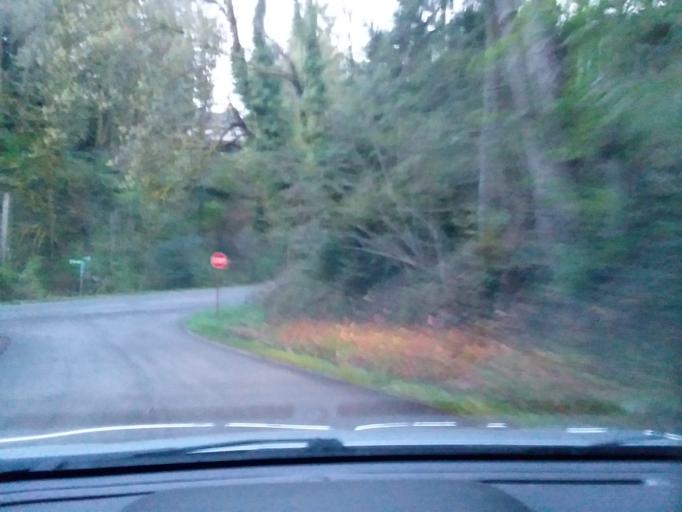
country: US
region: Washington
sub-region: King County
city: Lake Forest Park
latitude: 47.7613
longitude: -122.2983
